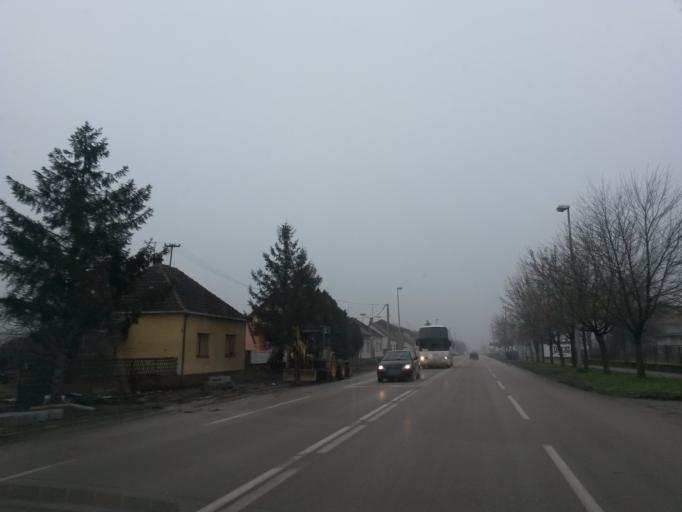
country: HR
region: Vukovarsko-Srijemska
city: Zupanja
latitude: 45.0804
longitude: 18.6955
